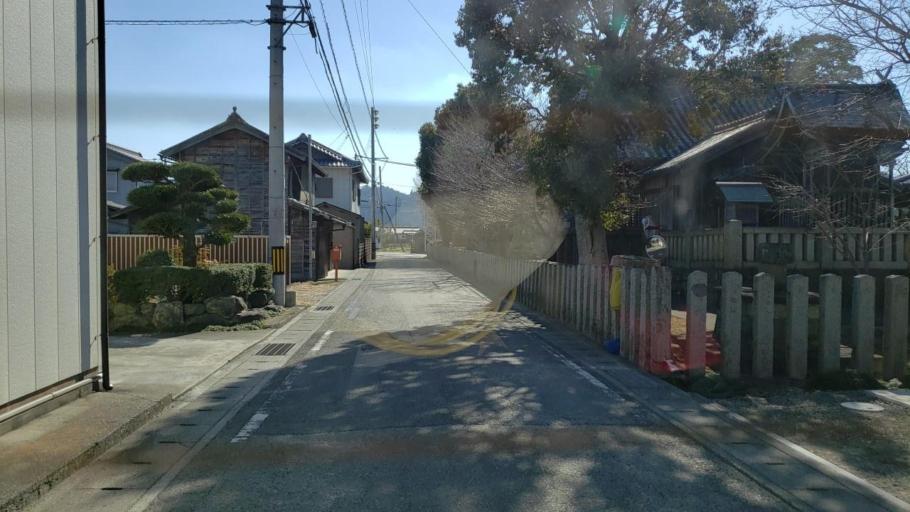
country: JP
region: Tokushima
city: Ishii
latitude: 34.0723
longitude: 134.4322
